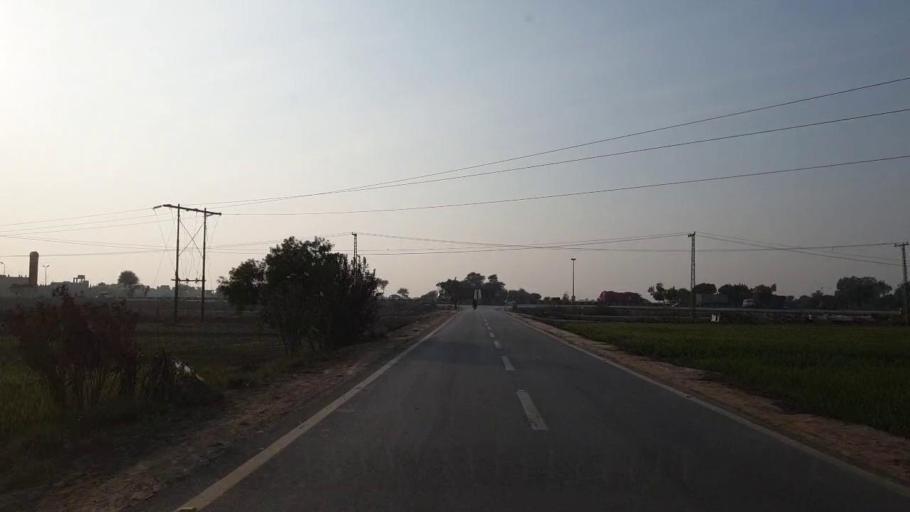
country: PK
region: Sindh
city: Matiari
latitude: 25.5875
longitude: 68.4430
